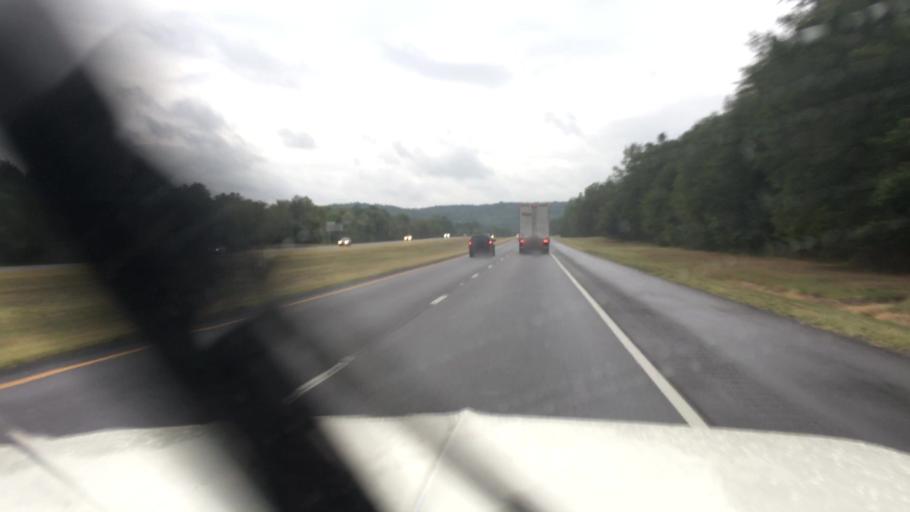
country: US
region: Alabama
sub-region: Morgan County
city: Falkville
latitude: 34.3526
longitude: -86.8921
